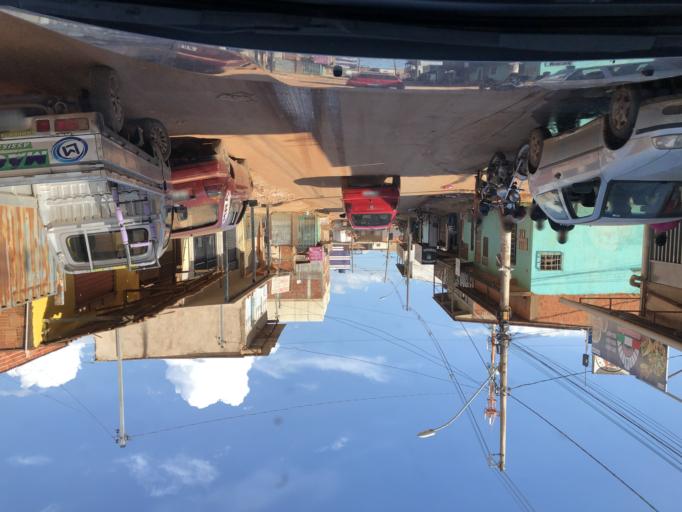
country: BR
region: Federal District
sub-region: Brasilia
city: Brasilia
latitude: -15.8181
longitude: -48.1538
